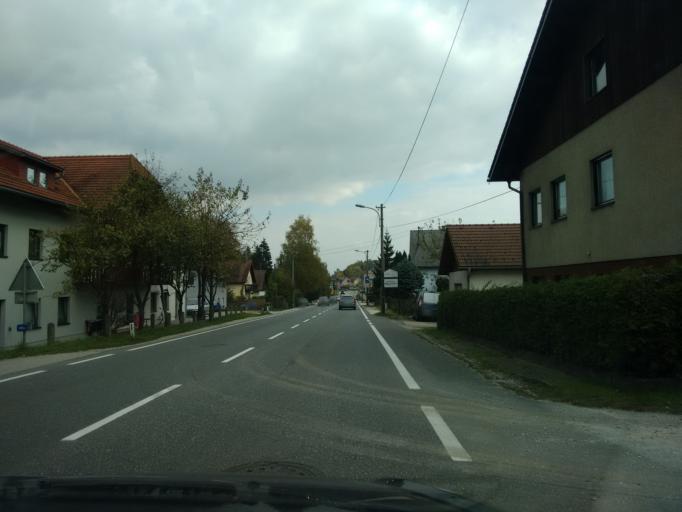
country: AT
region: Upper Austria
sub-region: Politischer Bezirk Vocklabruck
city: Attnang-Puchheim
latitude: 48.0061
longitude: 13.7028
